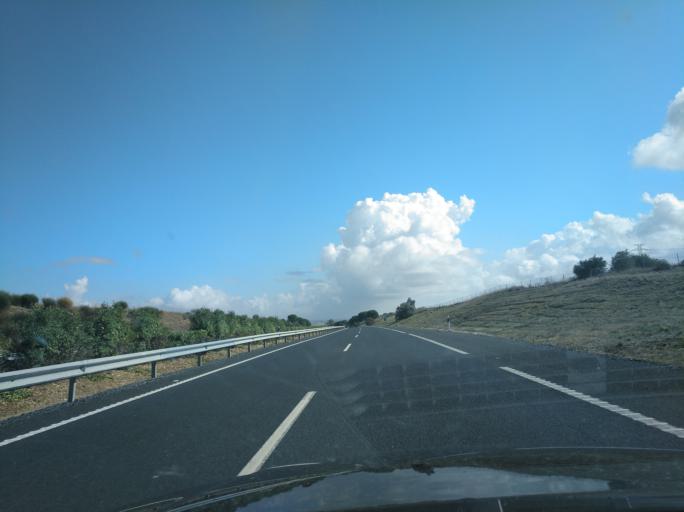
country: ES
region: Andalusia
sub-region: Provincia de Huelva
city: Chucena
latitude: 37.3536
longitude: -6.3709
